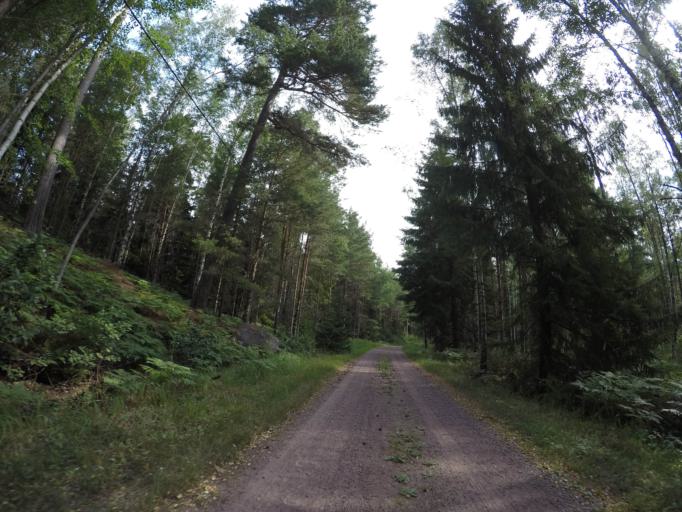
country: AX
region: Alands landsbygd
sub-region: Hammarland
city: Hammarland
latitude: 60.2254
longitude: 19.8368
